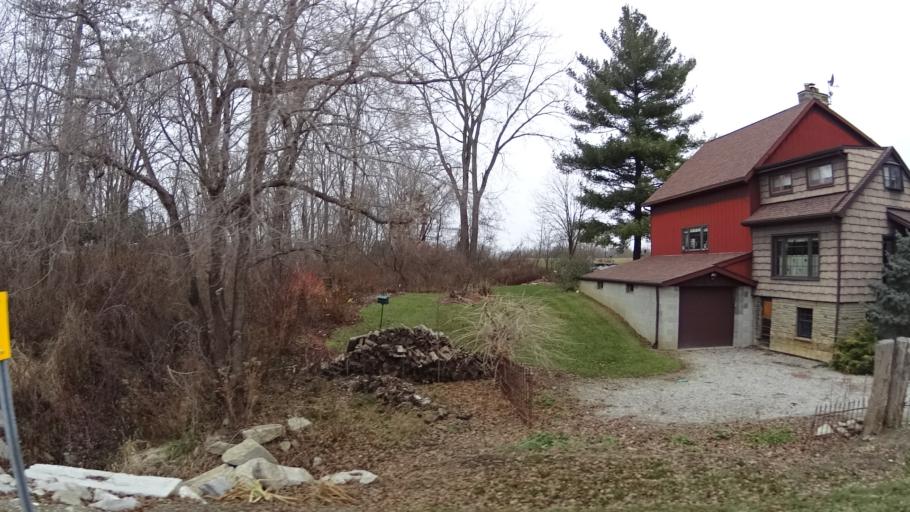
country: US
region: Ohio
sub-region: Lorain County
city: Wellington
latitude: 41.1491
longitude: -82.2691
